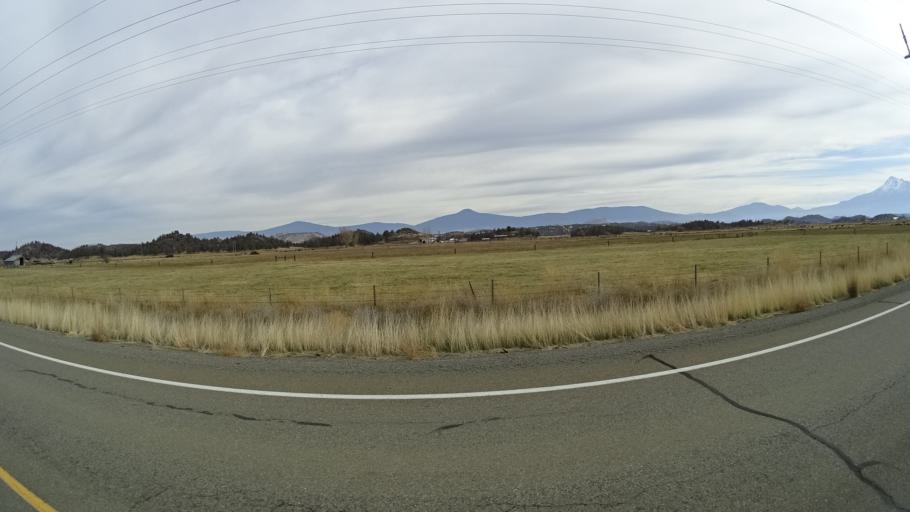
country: US
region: California
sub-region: Siskiyou County
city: Montague
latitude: 41.6703
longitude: -122.5241
